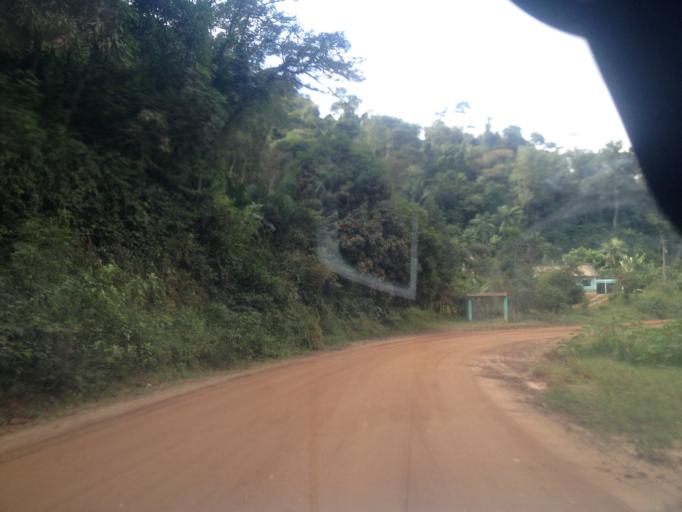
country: BR
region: Rio de Janeiro
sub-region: Quatis
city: Quatis
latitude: -22.2325
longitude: -44.2588
